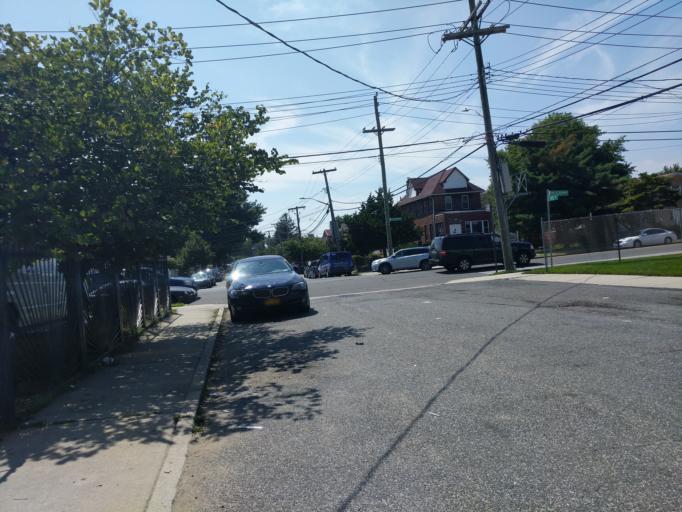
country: US
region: New York
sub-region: Queens County
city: Jamaica
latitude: 40.6661
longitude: -73.7697
